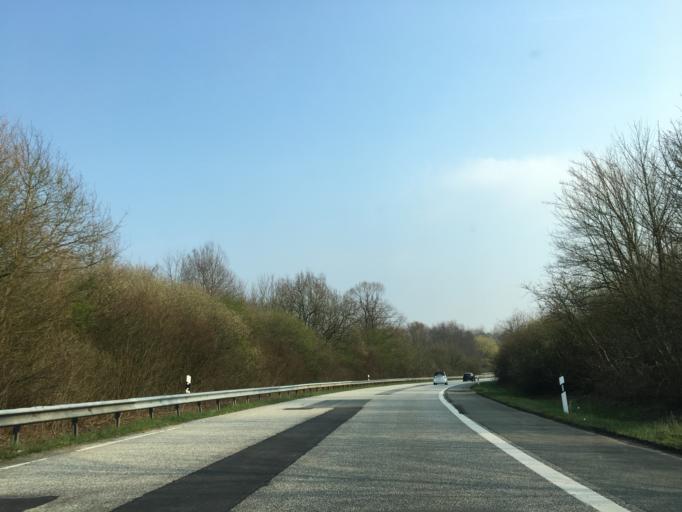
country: DE
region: Schleswig-Holstein
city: Kiel
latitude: 54.3501
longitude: 10.1185
